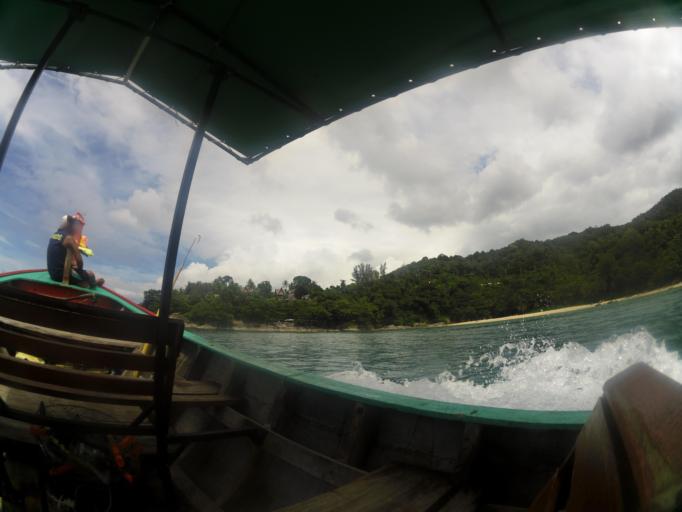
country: TH
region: Phuket
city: Patong
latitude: 7.9672
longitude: 98.2774
